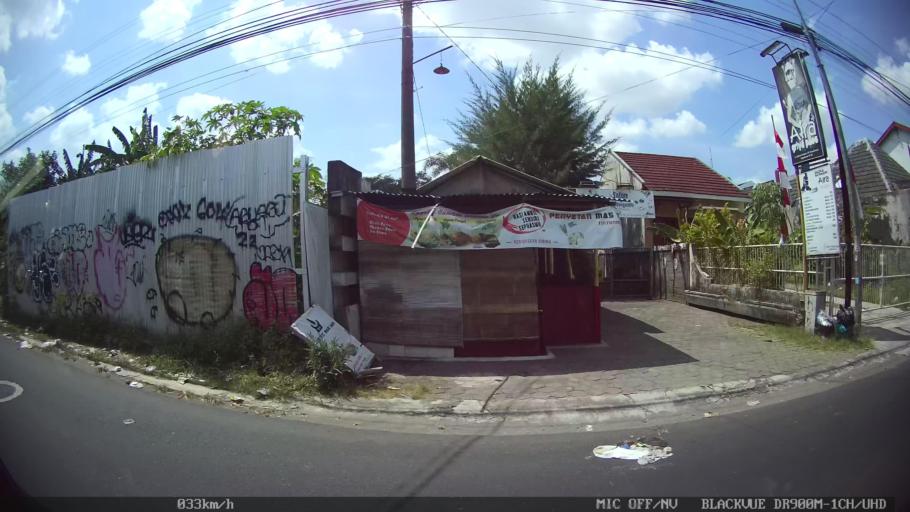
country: ID
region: Daerah Istimewa Yogyakarta
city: Kasihan
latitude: -7.8219
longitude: 110.3477
